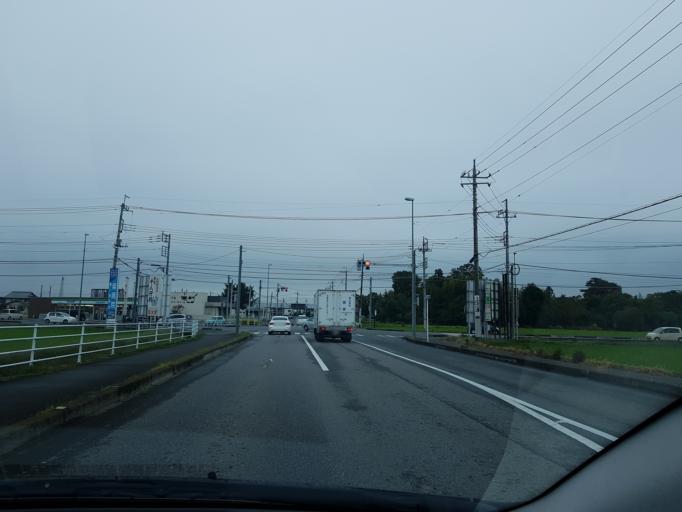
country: JP
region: Tochigi
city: Utsunomiya-shi
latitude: 36.5857
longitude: 139.8996
